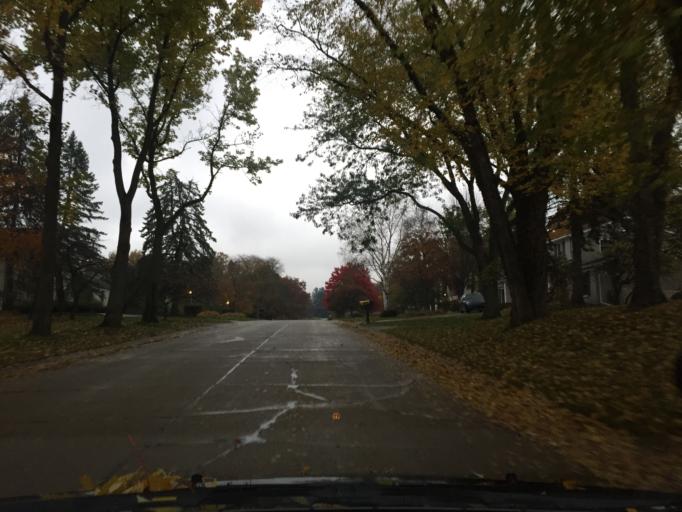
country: US
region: Michigan
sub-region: Oakland County
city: Bloomfield Hills
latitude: 42.5723
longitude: -83.2767
